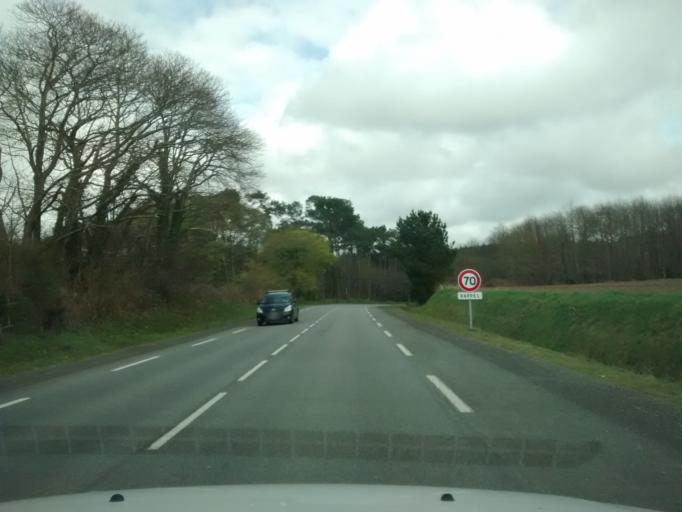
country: FR
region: Brittany
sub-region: Departement du Morbihan
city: Guidel-Plage
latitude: 47.8004
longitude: -3.5263
